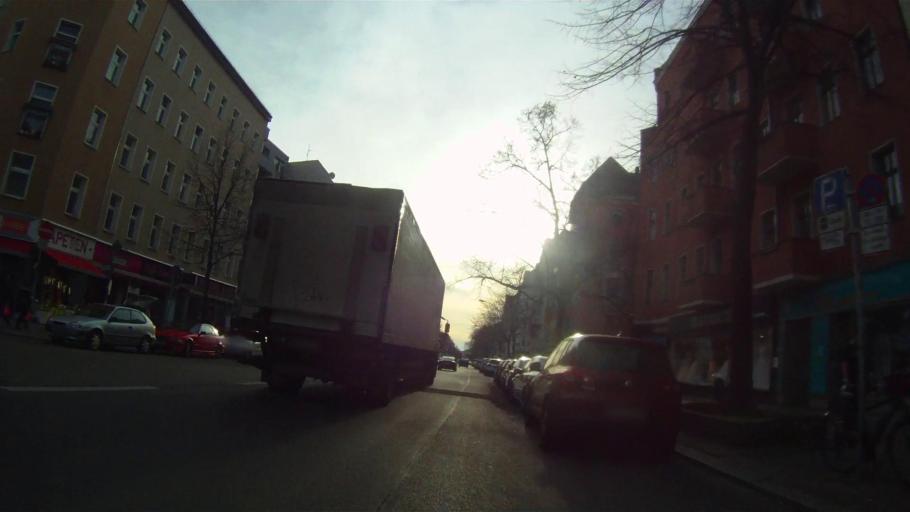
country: DE
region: Berlin
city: Berlin Treptow
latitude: 52.4756
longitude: 13.4272
